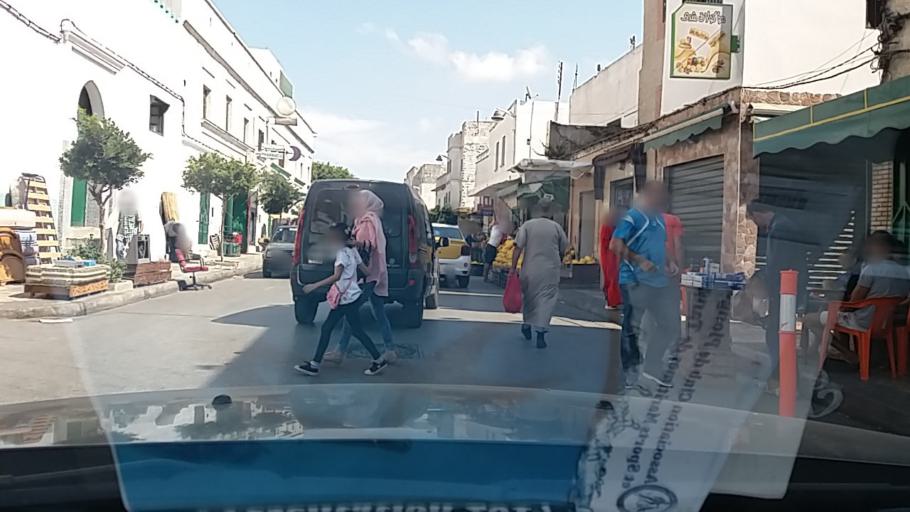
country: MA
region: Tanger-Tetouan
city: Tetouan
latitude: 35.5744
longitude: -5.3882
